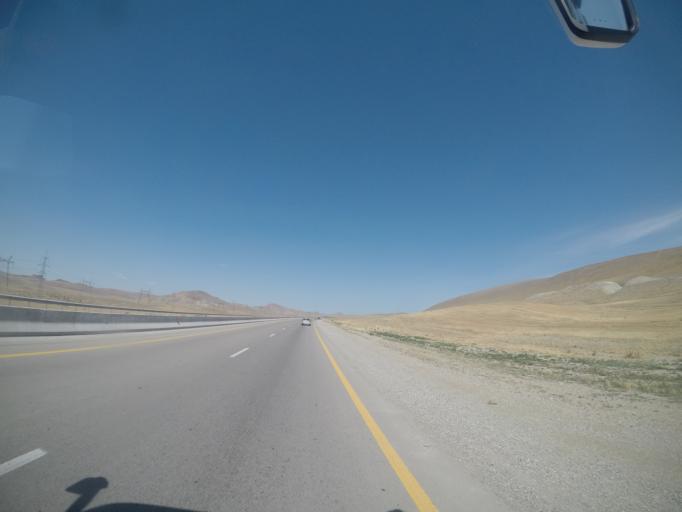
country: AZ
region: Sumqayit
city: Haci Zeynalabdin
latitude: 40.4947
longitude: 49.3249
